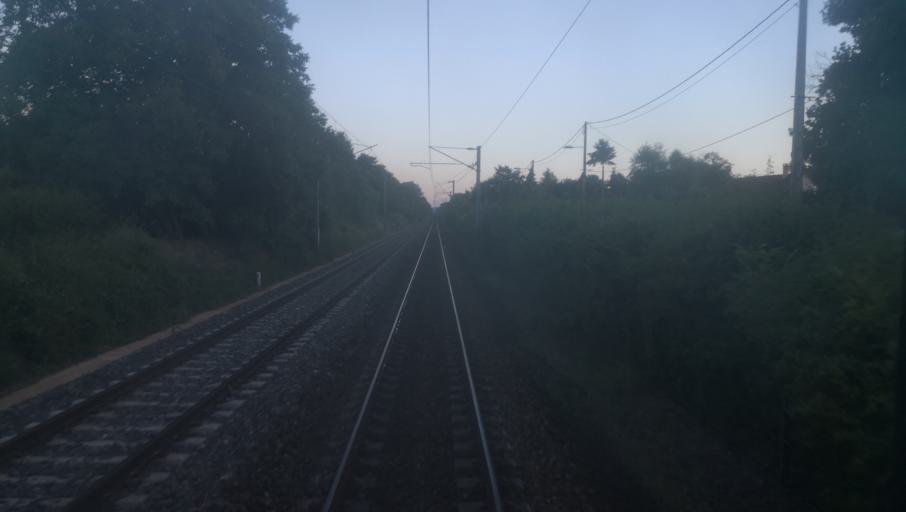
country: FR
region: Bourgogne
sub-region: Departement de la Nievre
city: Cosne-Cours-sur-Loire
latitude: 47.3687
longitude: 2.8973
